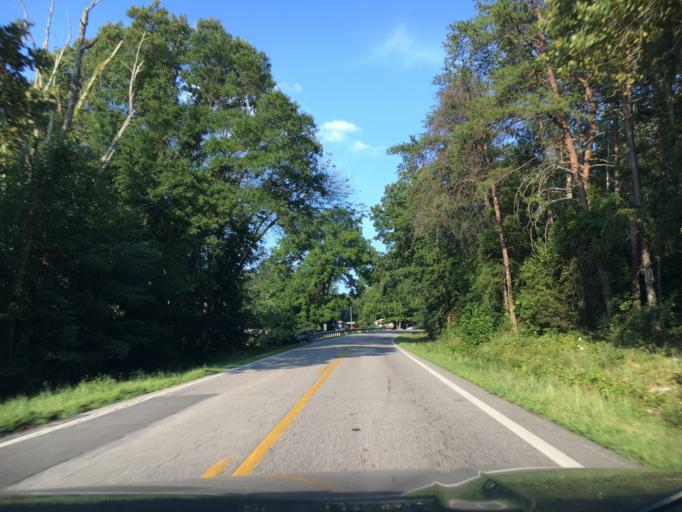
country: US
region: Virginia
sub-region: Pittsylvania County
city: Chatham
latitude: 36.8286
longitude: -79.2836
